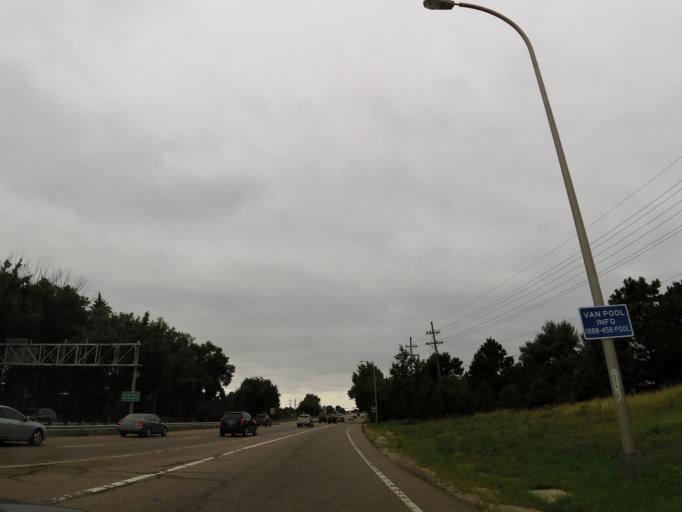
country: US
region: Colorado
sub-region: El Paso County
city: Colorado Springs
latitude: 38.7940
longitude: -104.8224
